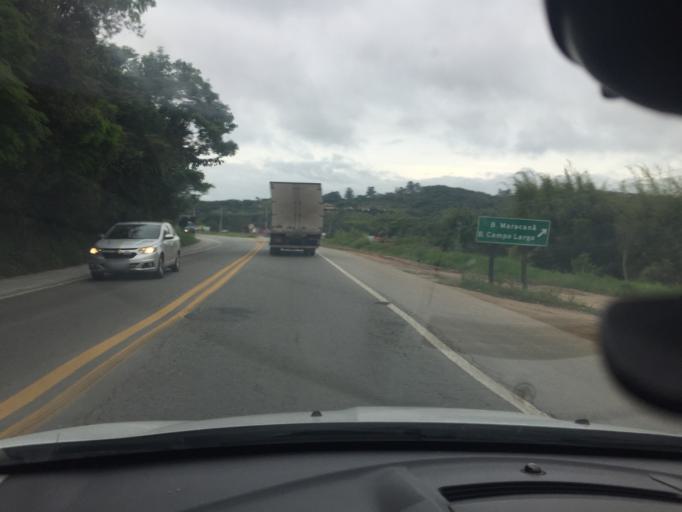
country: BR
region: Sao Paulo
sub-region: Jarinu
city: Jarinu
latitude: -23.1164
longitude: -46.7265
